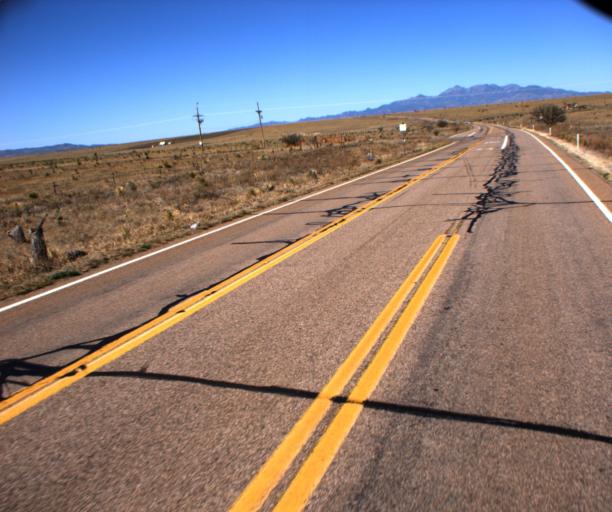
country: US
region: Arizona
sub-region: Cochise County
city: Huachuca City
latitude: 31.7240
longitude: -110.5233
